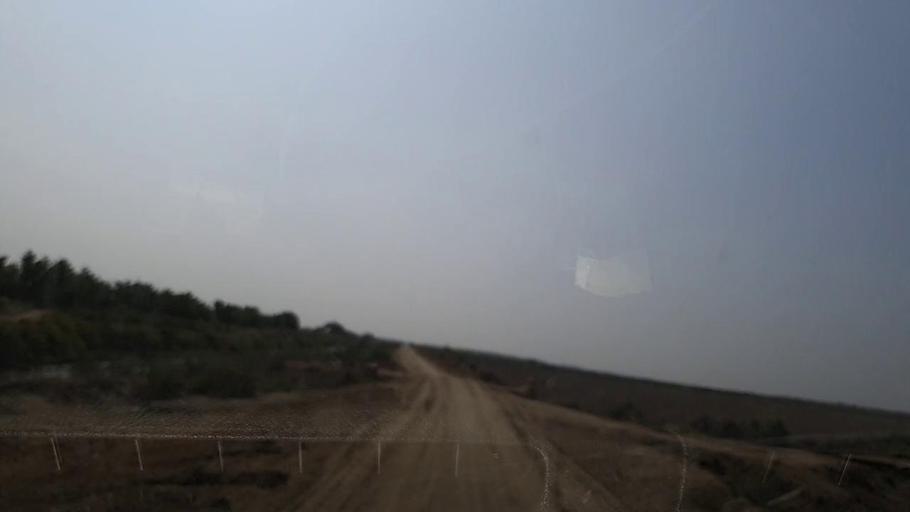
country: PK
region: Sindh
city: Mirpur Sakro
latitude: 24.5424
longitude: 67.7872
